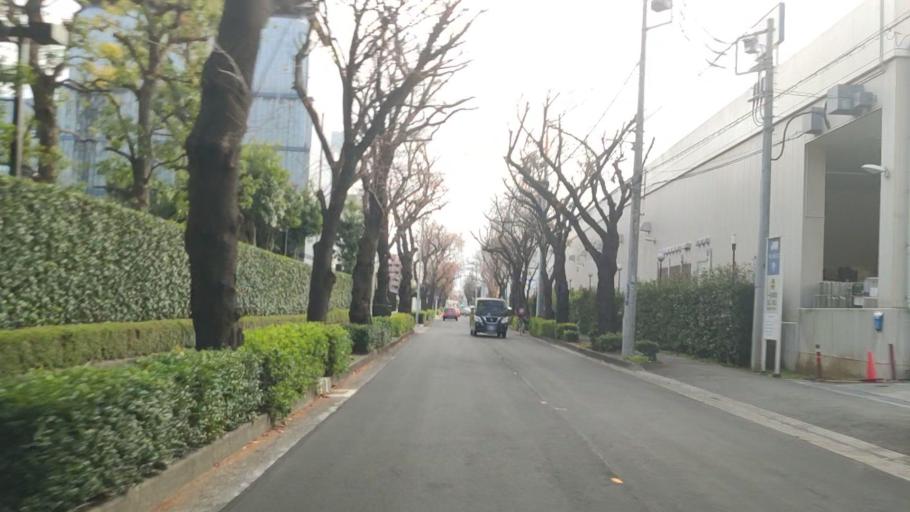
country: JP
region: Kanagawa
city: Minami-rinkan
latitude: 35.5043
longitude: 139.4516
